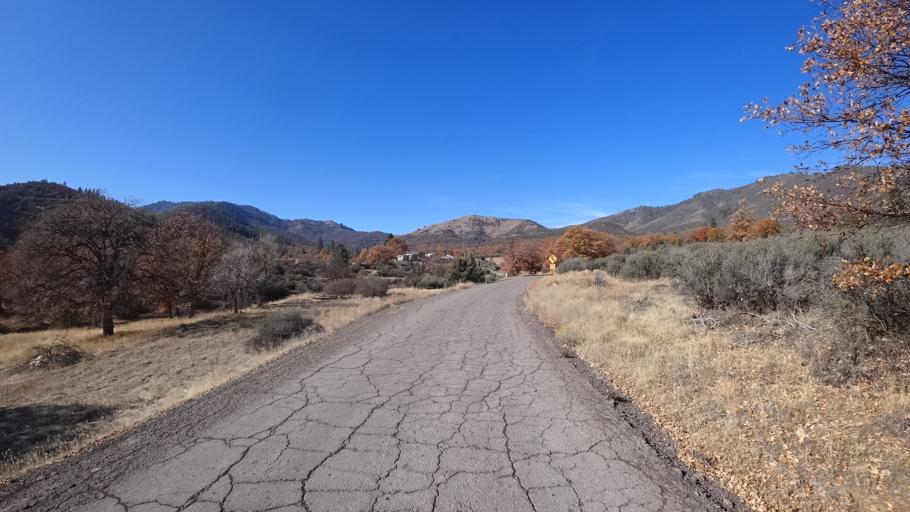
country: US
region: California
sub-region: Siskiyou County
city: Yreka
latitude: 41.7693
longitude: -122.6364
